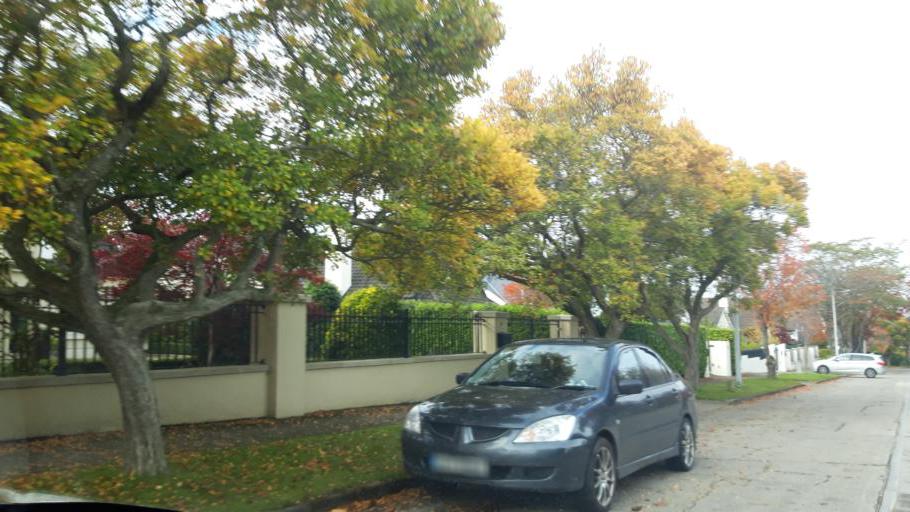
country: IE
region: Leinster
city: Mount Merrion
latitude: 53.2971
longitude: -6.2281
